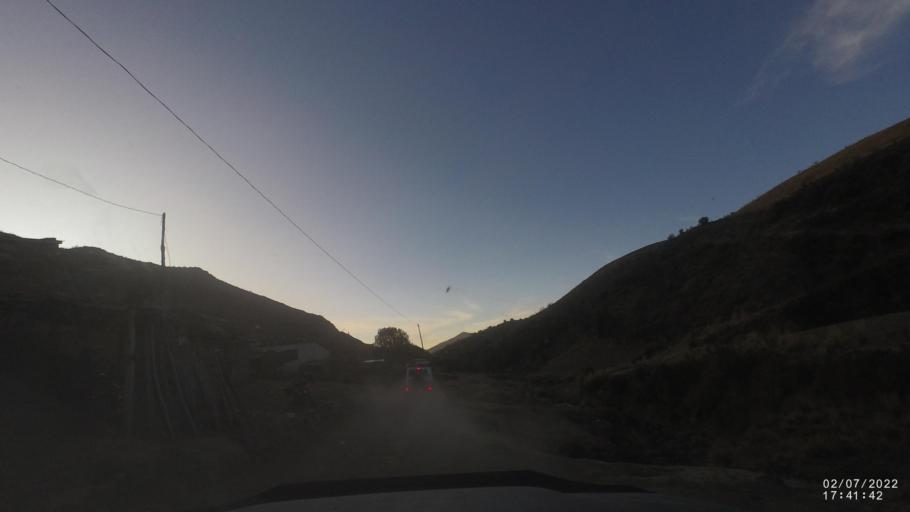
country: BO
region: Cochabamba
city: Irpa Irpa
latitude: -17.8605
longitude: -66.6141
